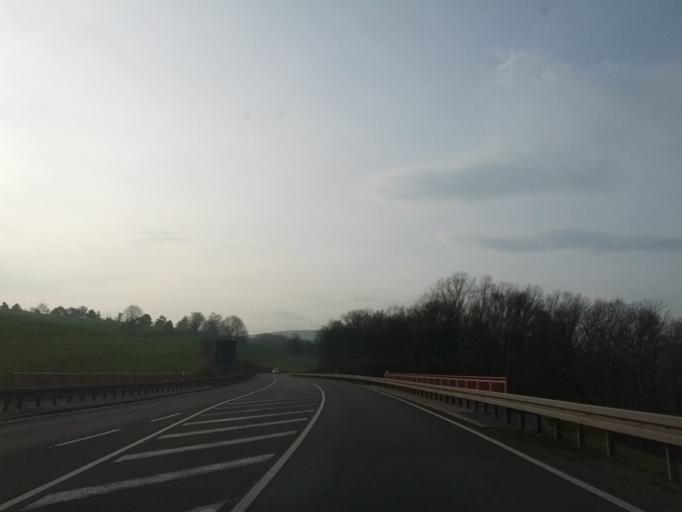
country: DE
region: Thuringia
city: Schwallungen
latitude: 50.6863
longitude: 10.3582
